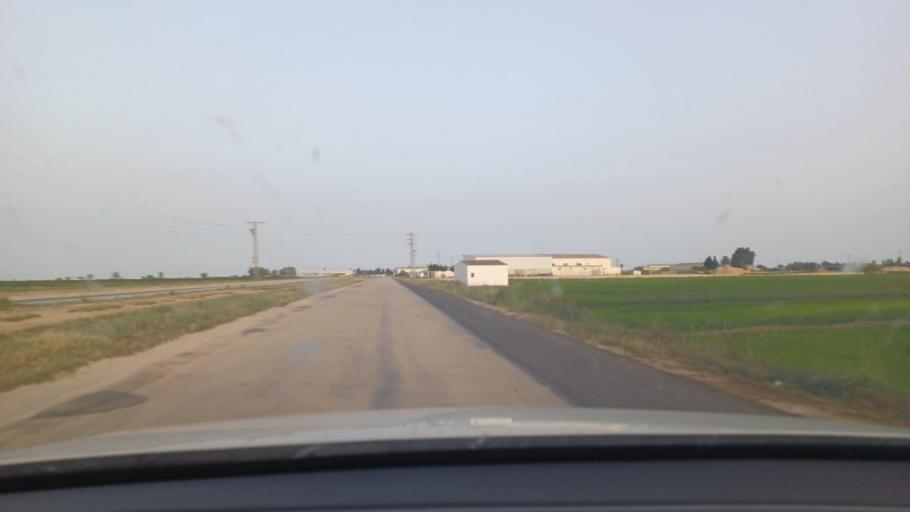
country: ES
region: Catalonia
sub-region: Provincia de Tarragona
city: Amposta
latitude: 40.7047
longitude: 0.5939
